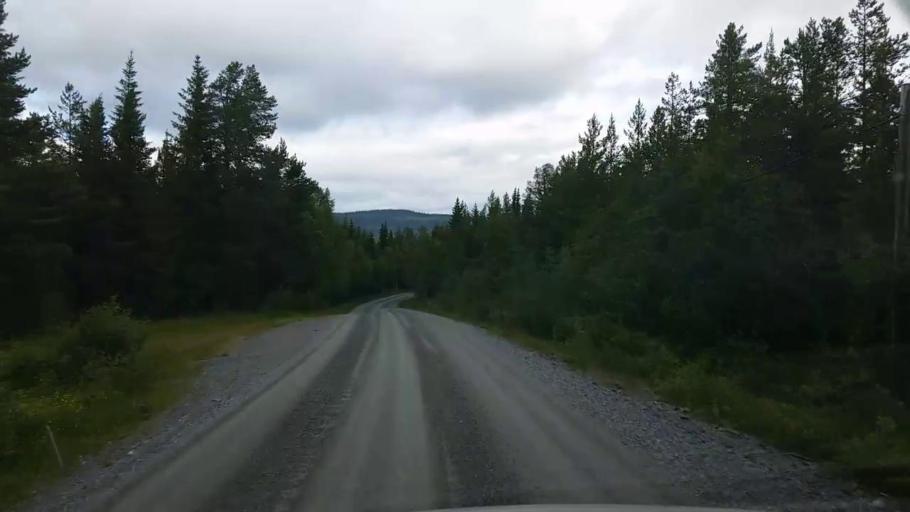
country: NO
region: Hedmark
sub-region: Engerdal
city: Engerdal
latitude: 62.4094
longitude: 12.6720
